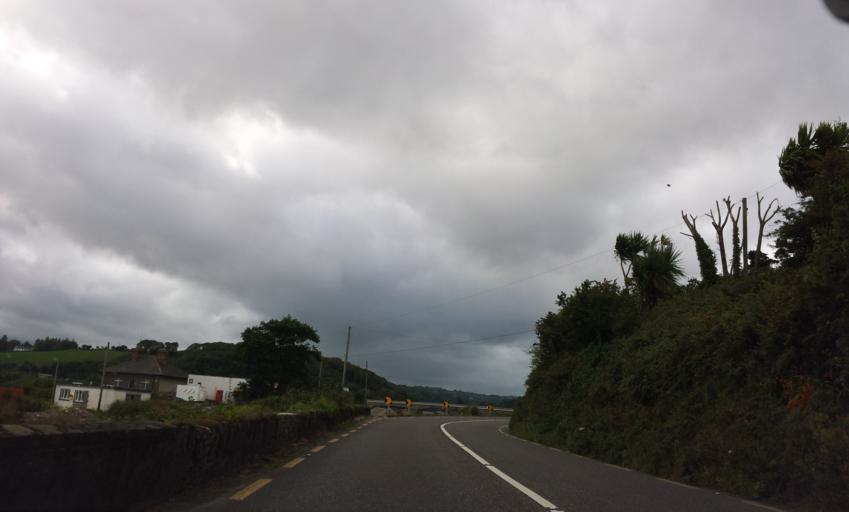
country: IE
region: Munster
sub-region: County Cork
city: Youghal
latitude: 51.9785
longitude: -7.8476
